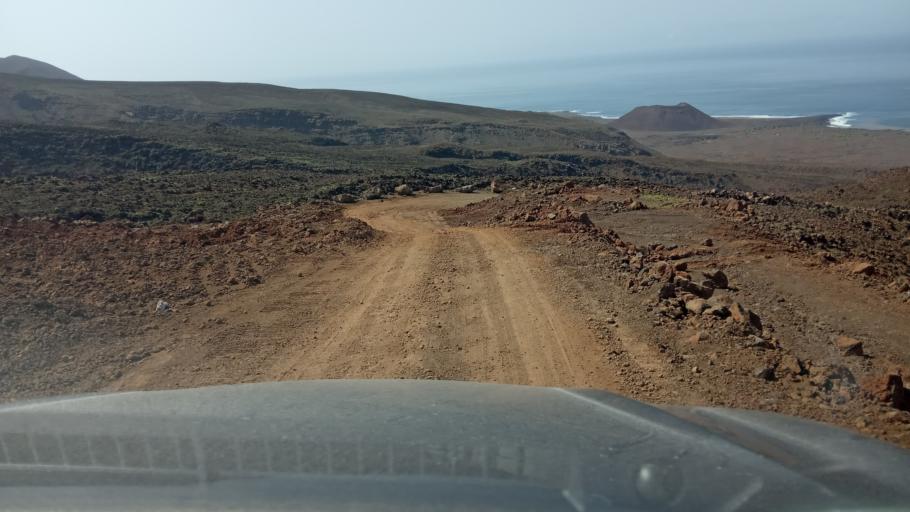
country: CV
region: Porto Novo
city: Porto Novo
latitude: 16.9472
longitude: -25.3051
